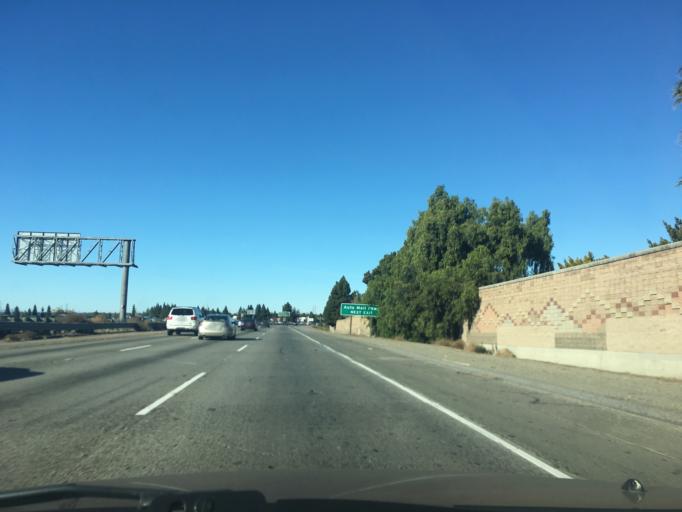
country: US
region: California
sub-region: Alameda County
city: Fremont
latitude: 37.5030
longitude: -121.9314
